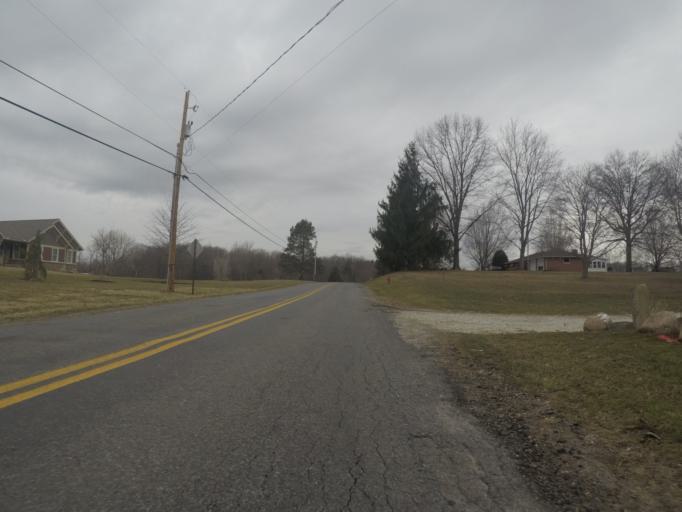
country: US
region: Ohio
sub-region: Portage County
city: Ravenna
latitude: 41.1796
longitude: -81.2954
